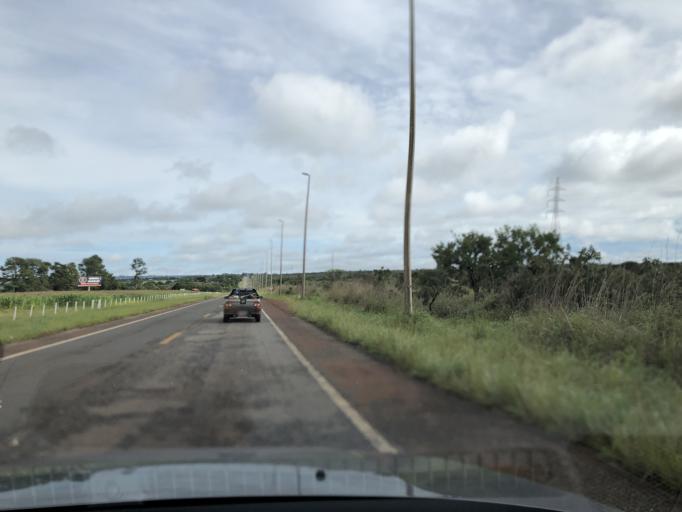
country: BR
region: Federal District
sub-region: Brasilia
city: Brasilia
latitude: -15.7190
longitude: -48.0868
